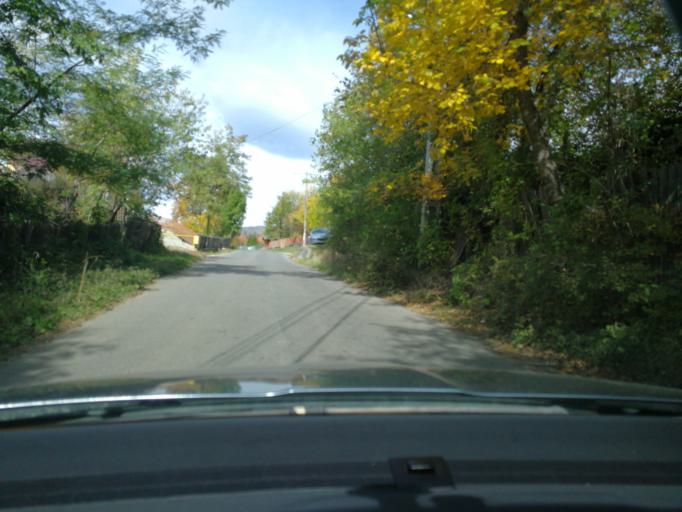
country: RO
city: Brebu Manastirei
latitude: 45.1861
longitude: 25.7662
